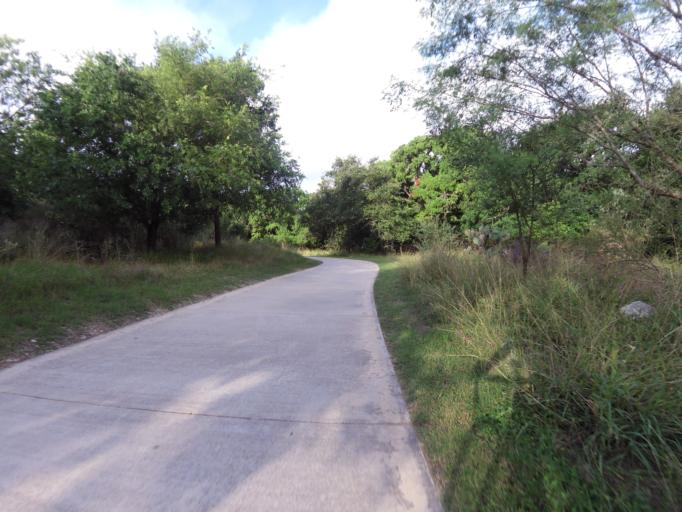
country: US
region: Texas
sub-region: Bexar County
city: Leon Valley
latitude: 29.5077
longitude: -98.6367
